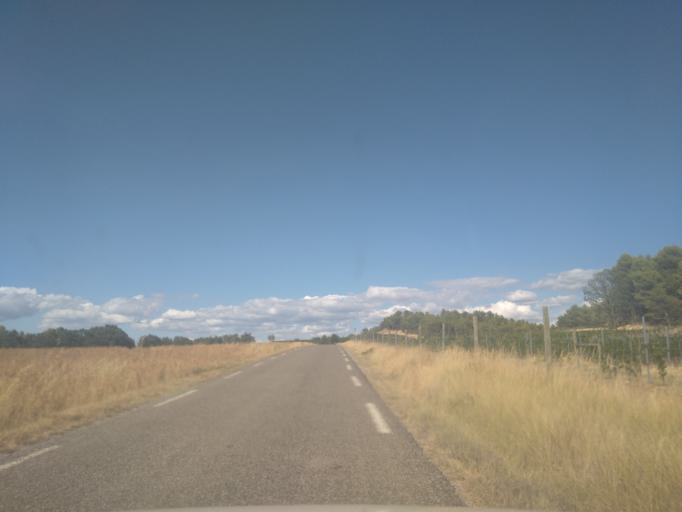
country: FR
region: Provence-Alpes-Cote d'Azur
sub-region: Departement du Var
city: Regusse
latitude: 43.6950
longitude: 6.1174
